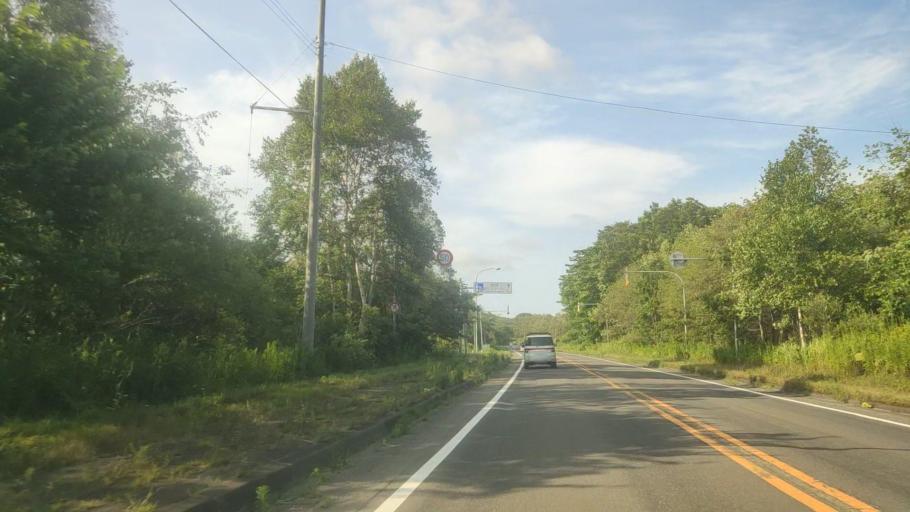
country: JP
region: Hokkaido
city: Chitose
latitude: 42.8602
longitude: 141.8219
